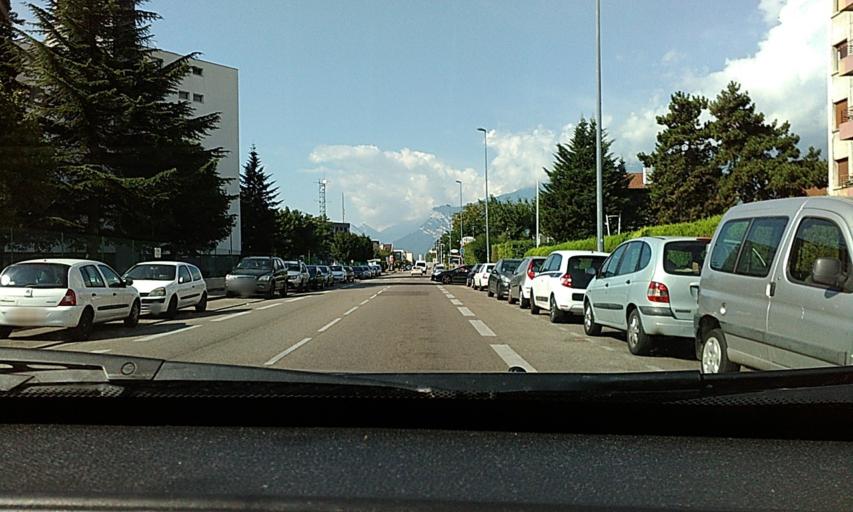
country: FR
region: Rhone-Alpes
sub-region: Departement de l'Isere
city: Grenoble
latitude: 45.1687
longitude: 5.7219
